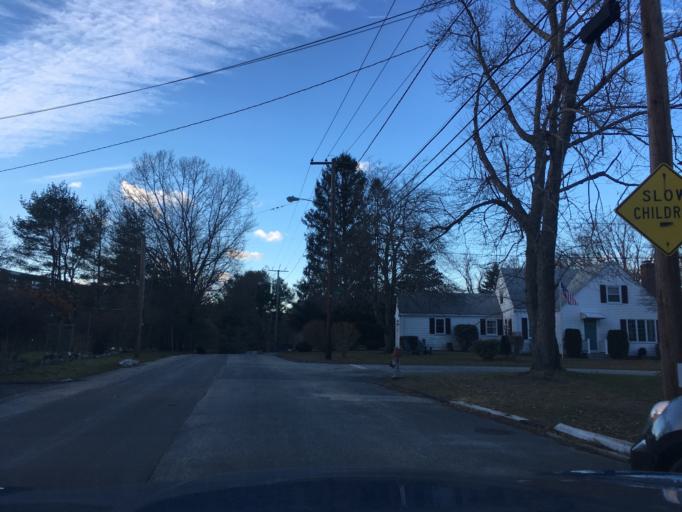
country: US
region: Rhode Island
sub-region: Kent County
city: East Greenwich
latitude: 41.6538
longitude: -71.4598
